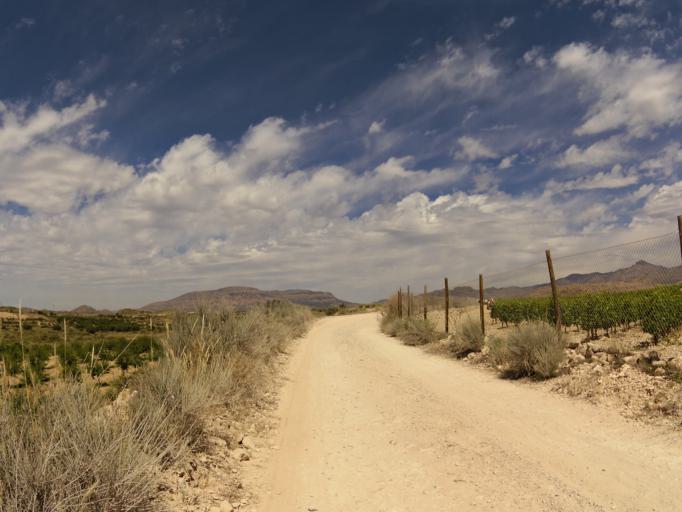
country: ES
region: Valencia
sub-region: Provincia de Alicante
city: Agost
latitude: 38.4021
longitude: -0.6096
